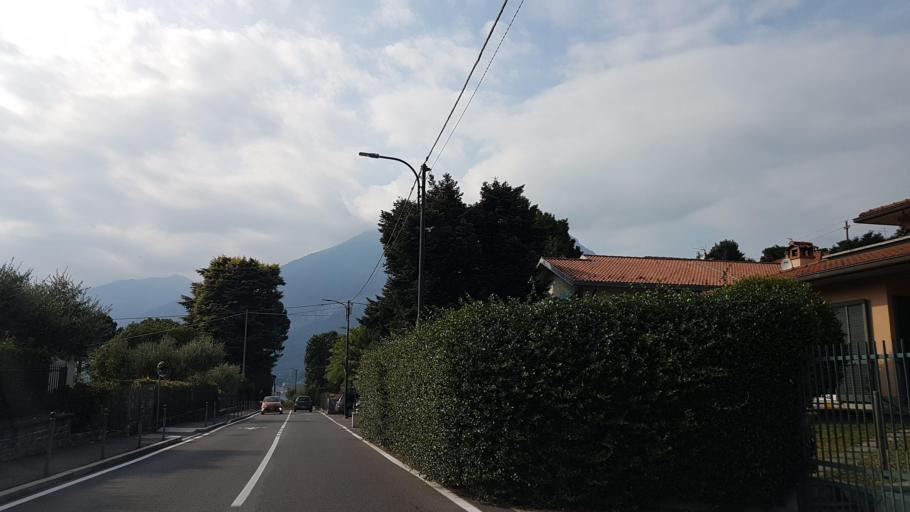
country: IT
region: Lombardy
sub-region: Provincia di Como
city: Bellagio
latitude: 45.9784
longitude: 9.2581
